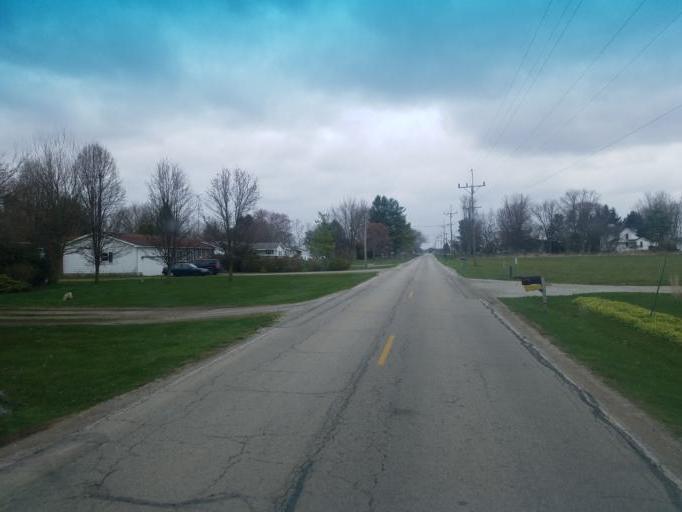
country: US
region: Ohio
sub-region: Marion County
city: Prospect
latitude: 40.4983
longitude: -83.1516
